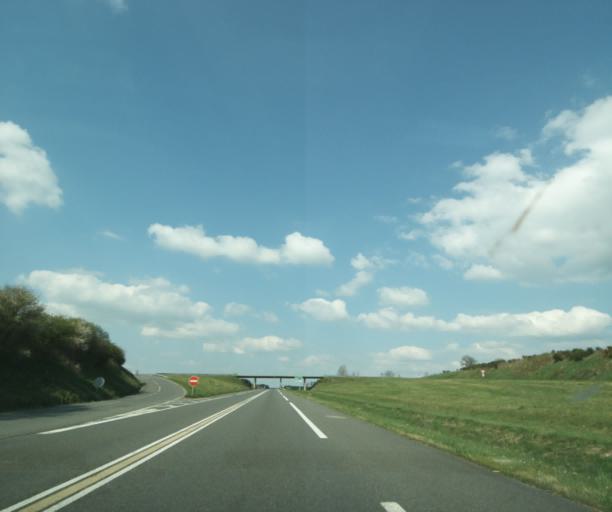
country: FR
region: Auvergne
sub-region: Departement de l'Allier
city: Montmarault
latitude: 46.3744
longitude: 3.0288
